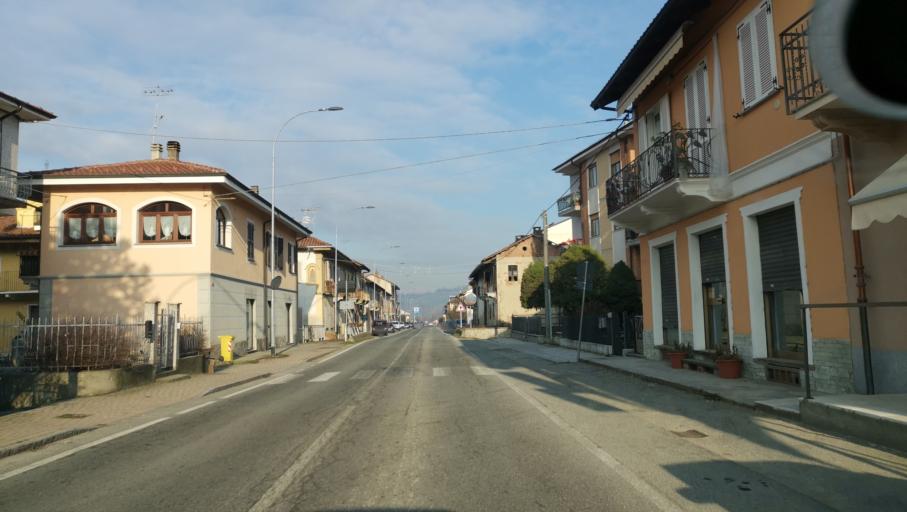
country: IT
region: Piedmont
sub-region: Provincia di Torino
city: Casalborgone
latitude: 45.1311
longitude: 7.9421
